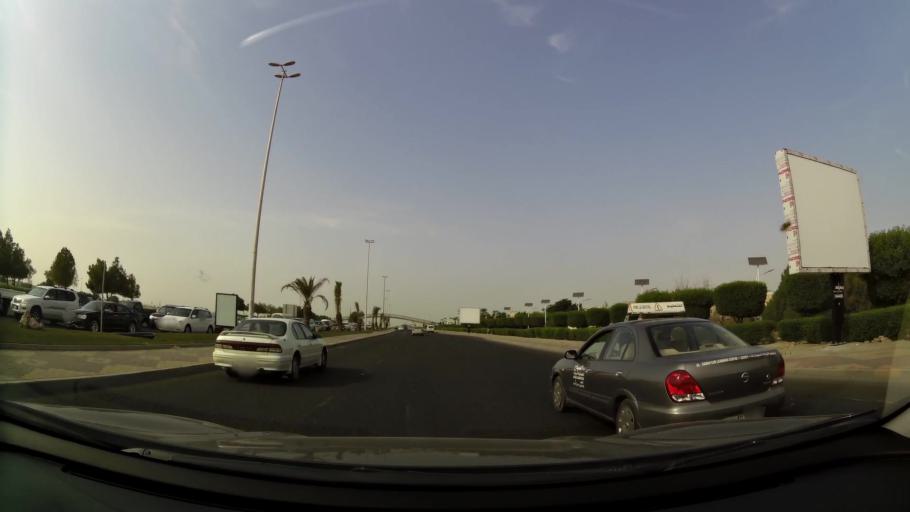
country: KW
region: Al Asimah
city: Ash Shamiyah
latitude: 29.3194
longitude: 47.9604
